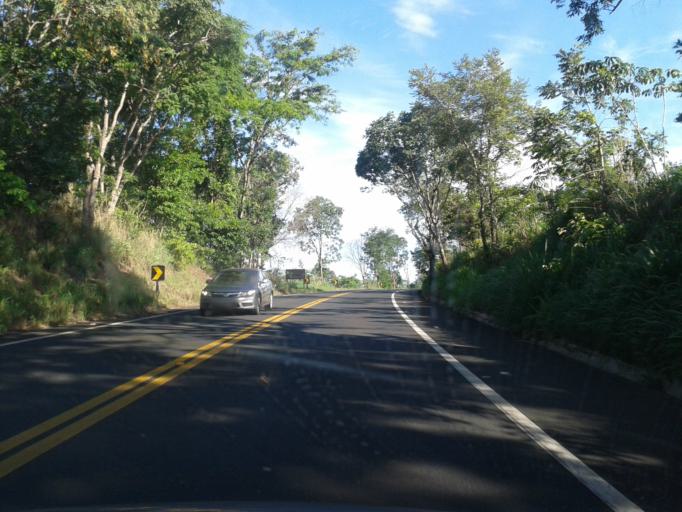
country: BR
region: Goias
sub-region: Caldas Novas
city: Caldas Novas
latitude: -18.1097
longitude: -48.6162
